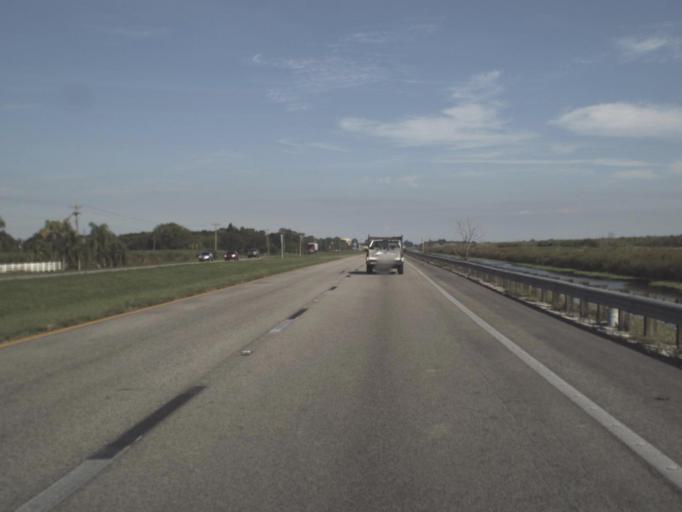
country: US
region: Florida
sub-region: Hendry County
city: Harlem
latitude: 26.7541
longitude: -80.9907
